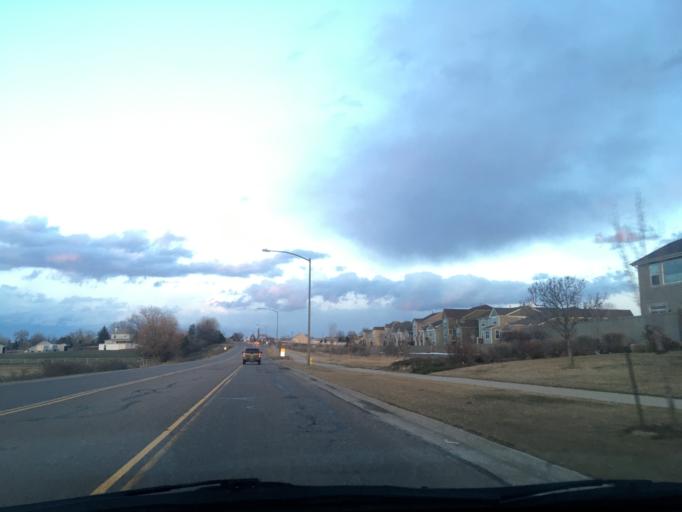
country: US
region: Colorado
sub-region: Adams County
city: Todd Creek
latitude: 39.9574
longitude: -104.9507
